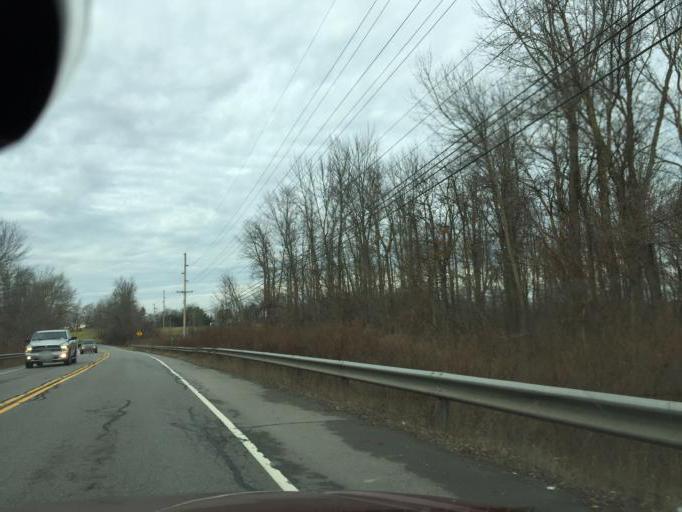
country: US
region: New York
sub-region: Monroe County
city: Scottsville
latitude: 43.0921
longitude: -77.7307
